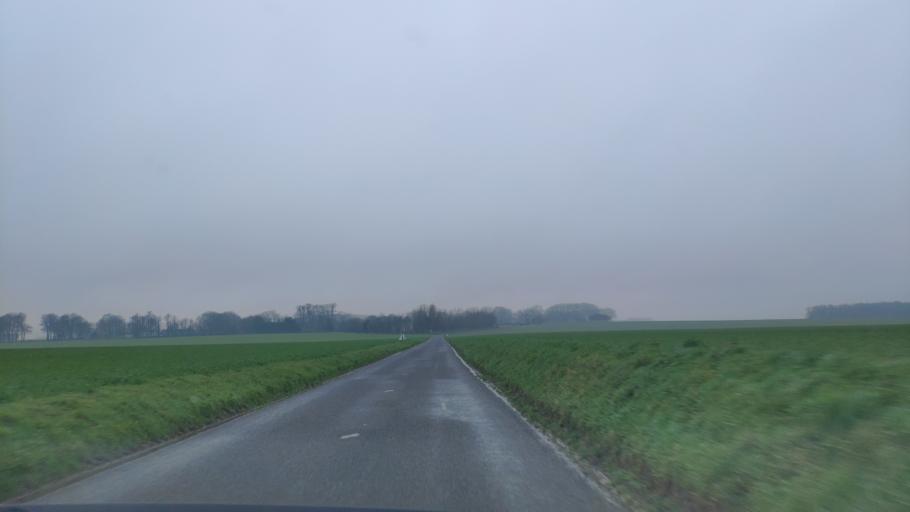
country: FR
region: Haute-Normandie
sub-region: Departement de la Seine-Maritime
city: Neville
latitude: 49.7754
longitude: 0.7192
